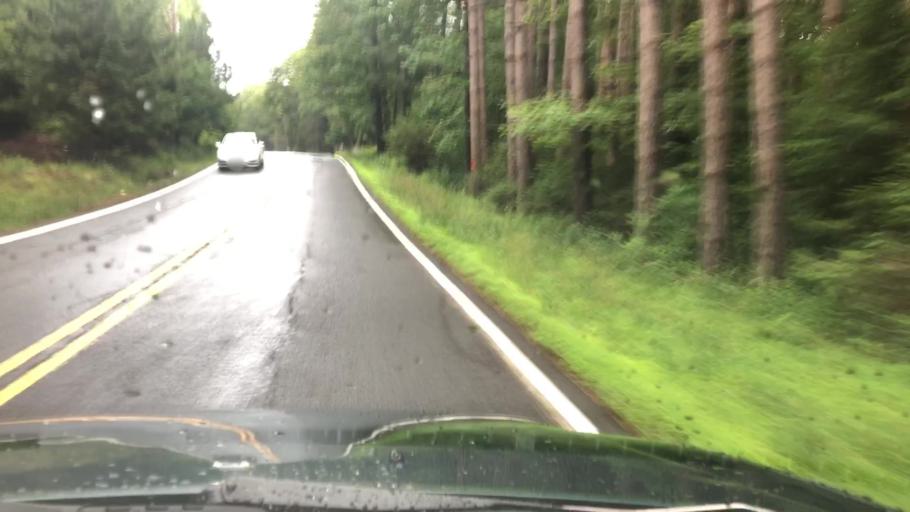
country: US
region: Pennsylvania
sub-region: Monroe County
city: Mountainhome
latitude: 41.2876
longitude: -75.2431
